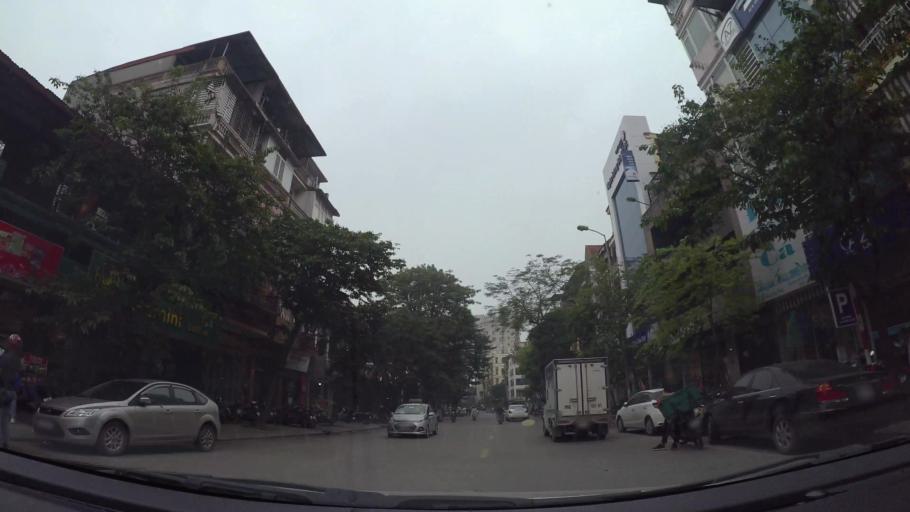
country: VN
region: Ha Noi
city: Dong Da
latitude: 21.0326
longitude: 105.8272
